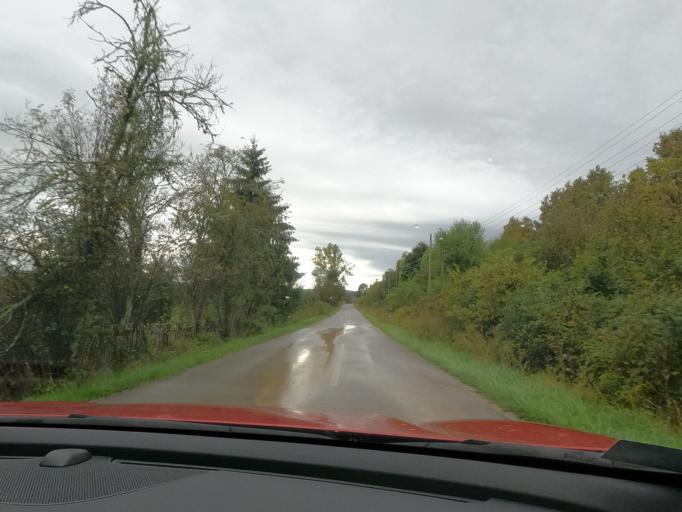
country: HR
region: Sisacko-Moslavacka
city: Glina
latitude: 45.3106
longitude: 16.1892
